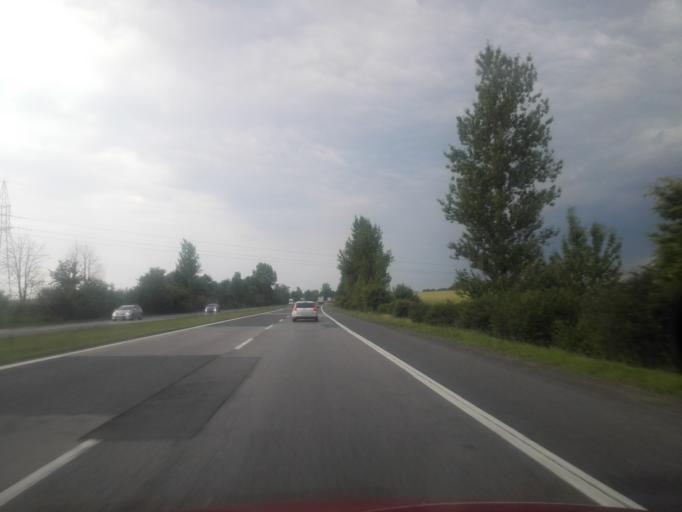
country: PL
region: Silesian Voivodeship
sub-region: Powiat czestochowski
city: Redziny
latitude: 50.8610
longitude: 19.1540
